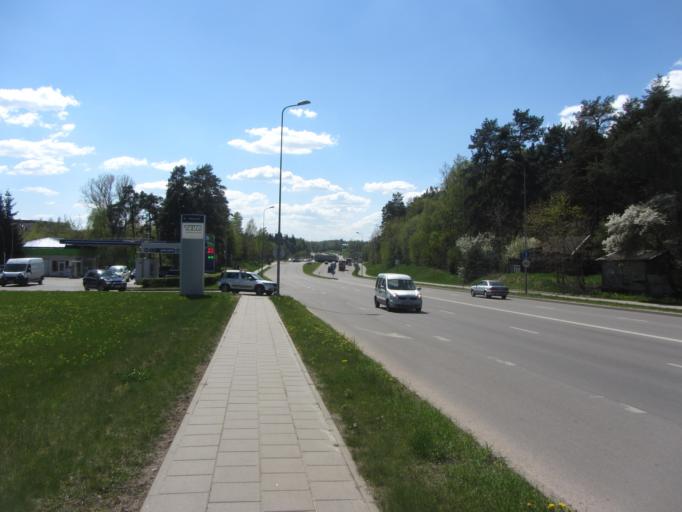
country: LT
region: Vilnius County
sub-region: Vilnius
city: Fabijoniskes
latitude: 54.7557
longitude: 25.2717
